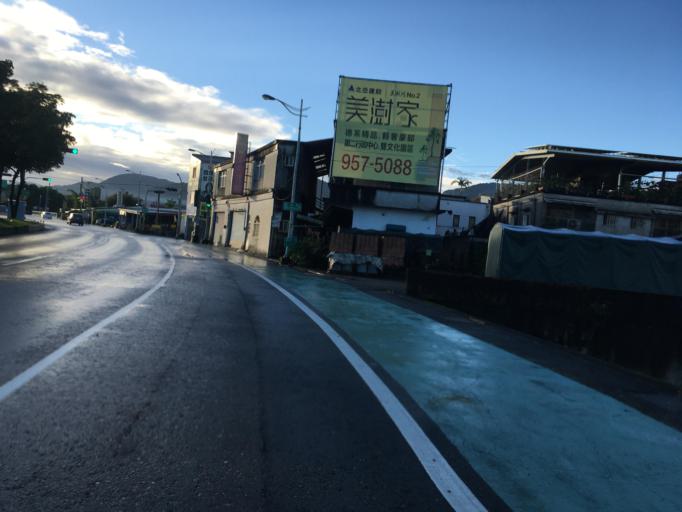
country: TW
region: Taiwan
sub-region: Yilan
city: Yilan
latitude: 24.6355
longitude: 121.7874
